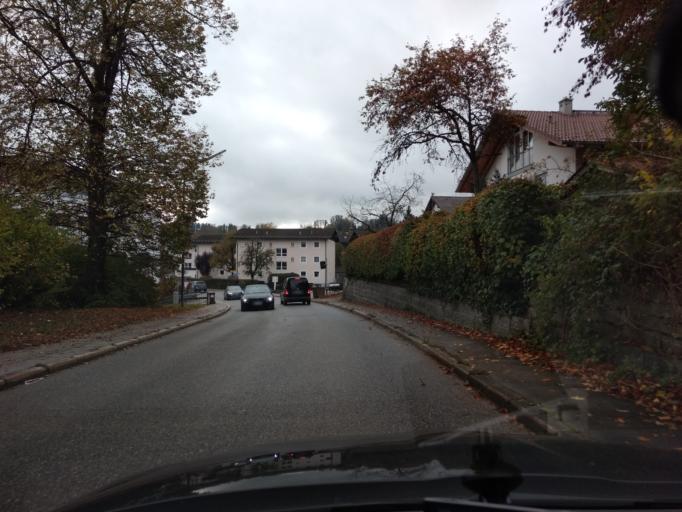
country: DE
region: Bavaria
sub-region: Upper Bavaria
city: Bad Toelz
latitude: 47.7650
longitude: 11.5392
